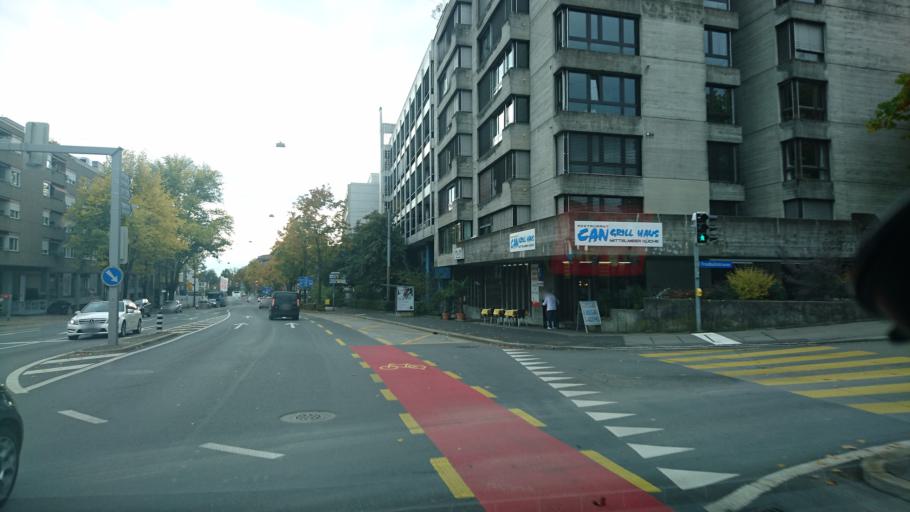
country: CH
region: Bern
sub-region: Bern-Mittelland District
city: Bern
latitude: 46.9501
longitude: 7.4245
